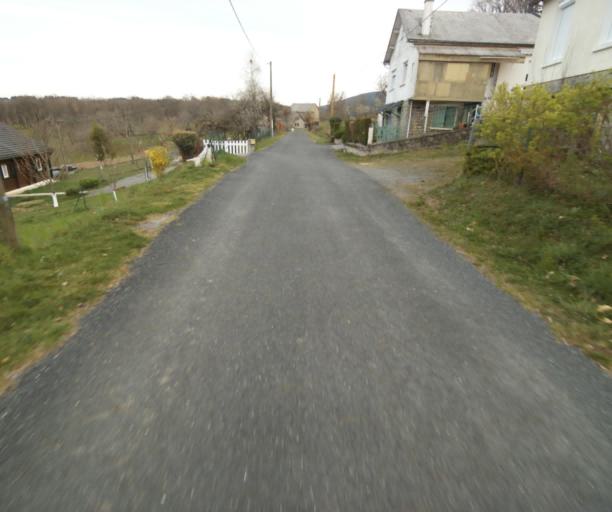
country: FR
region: Limousin
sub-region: Departement de la Correze
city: Correze
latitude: 45.4283
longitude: 1.8323
